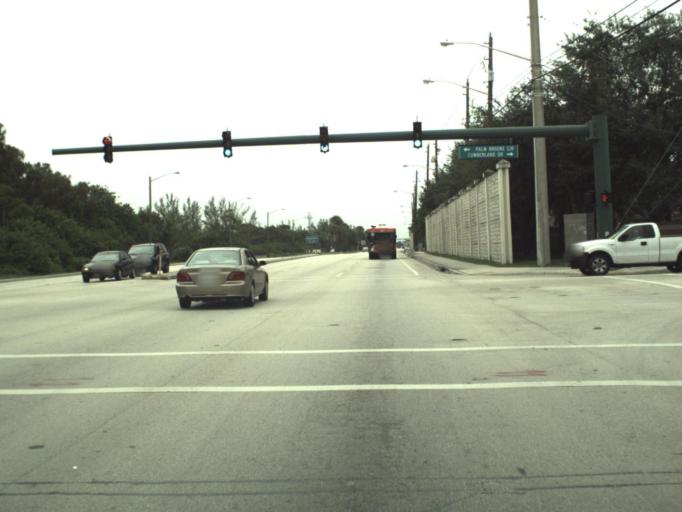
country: US
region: Florida
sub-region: Palm Beach County
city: Schall Circle
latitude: 26.7487
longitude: -80.1092
